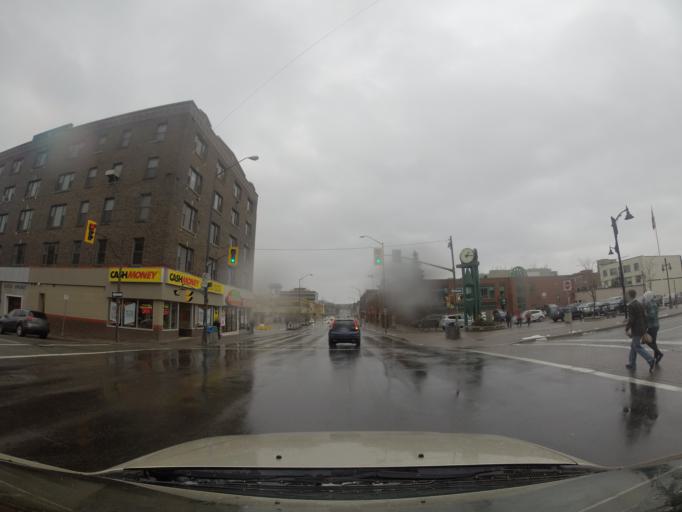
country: CA
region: Ontario
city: Greater Sudbury
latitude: 46.4931
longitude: -80.9954
